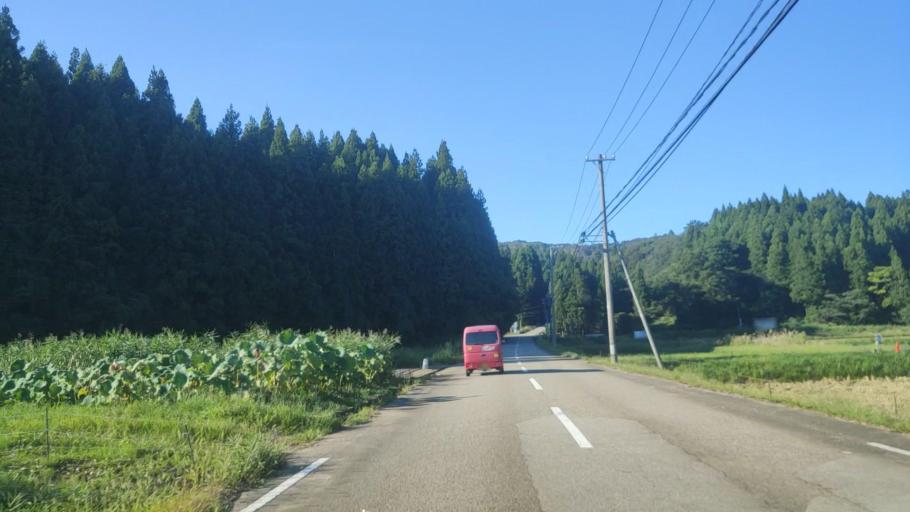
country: JP
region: Ishikawa
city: Nanao
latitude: 37.1075
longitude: 136.9620
